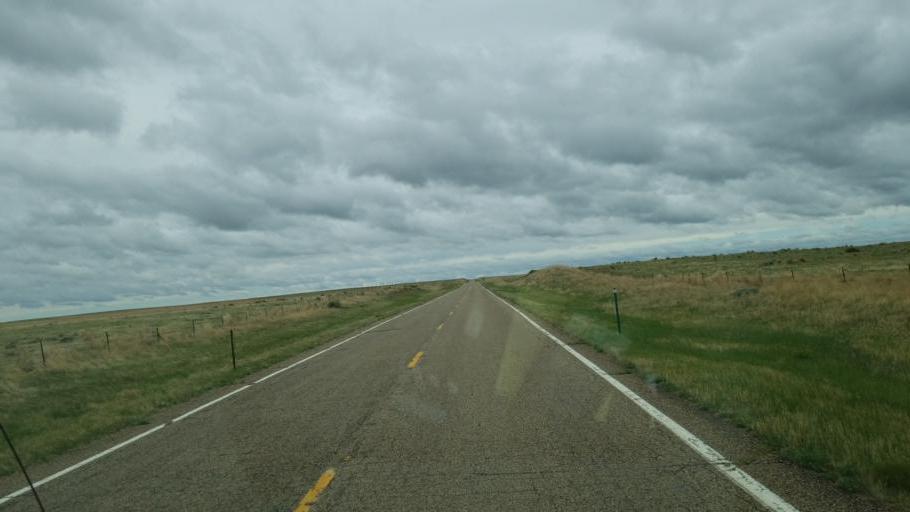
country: US
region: Colorado
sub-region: Lincoln County
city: Hugo
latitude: 38.8508
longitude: -103.5678
